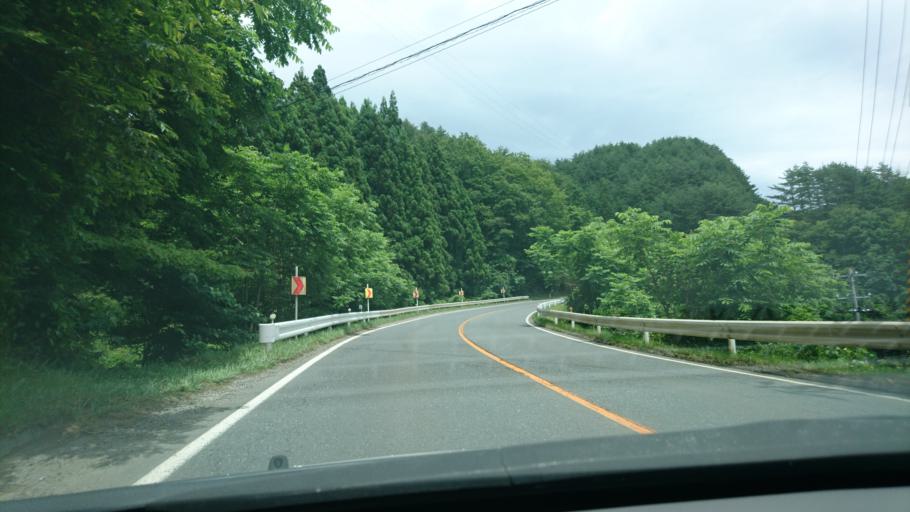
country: JP
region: Iwate
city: Miyako
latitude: 39.7042
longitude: 141.9581
